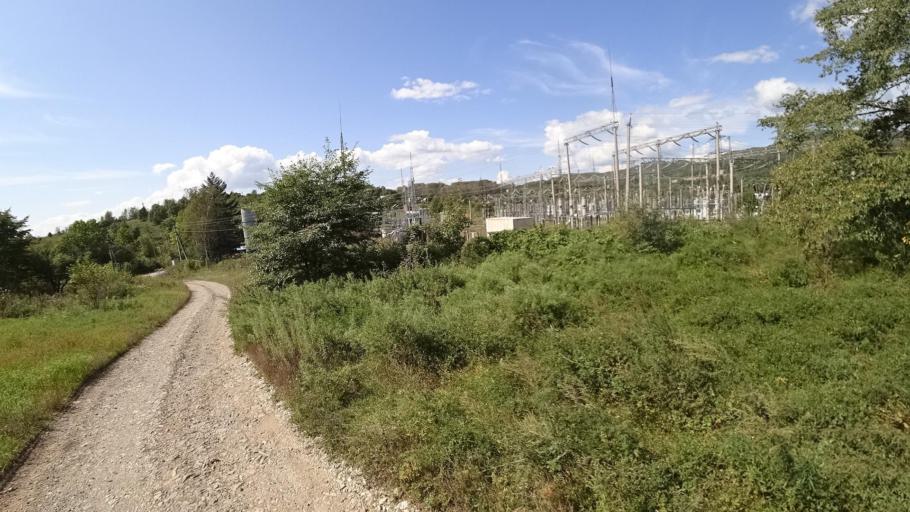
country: RU
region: Jewish Autonomous Oblast
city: Londoko
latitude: 49.0131
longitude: 131.8979
